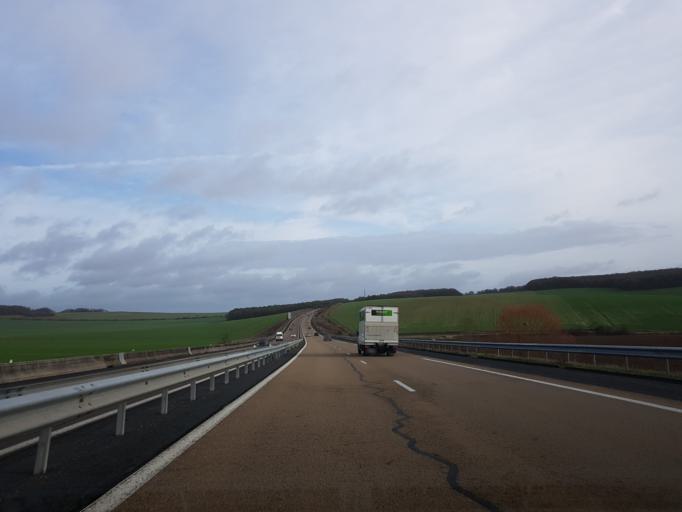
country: FR
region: Champagne-Ardenne
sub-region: Departement de l'Aube
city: Aix-en-Othe
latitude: 48.2609
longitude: 3.6758
